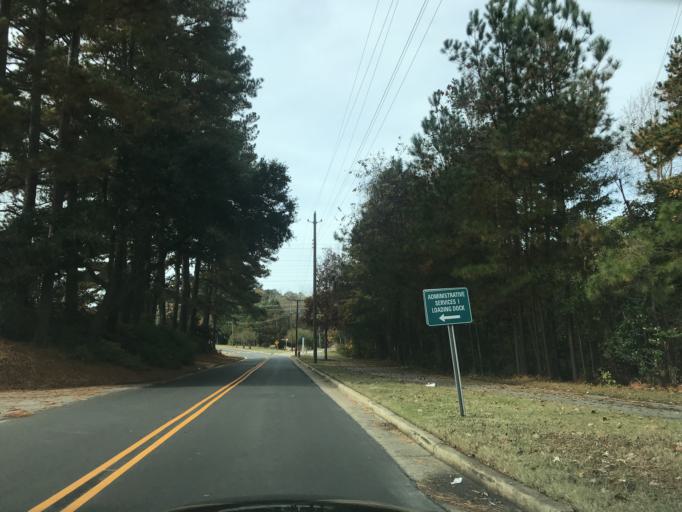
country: US
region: North Carolina
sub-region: Wake County
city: West Raleigh
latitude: 35.7881
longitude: -78.6832
